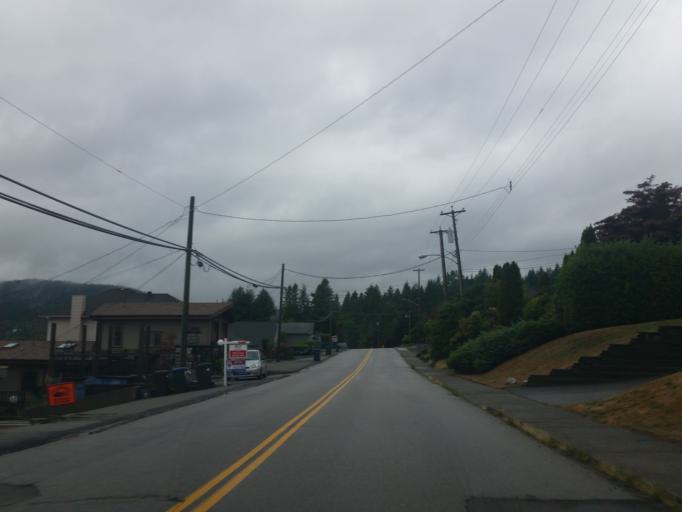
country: CA
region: British Columbia
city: Port Moody
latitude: 49.2973
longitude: -122.8617
